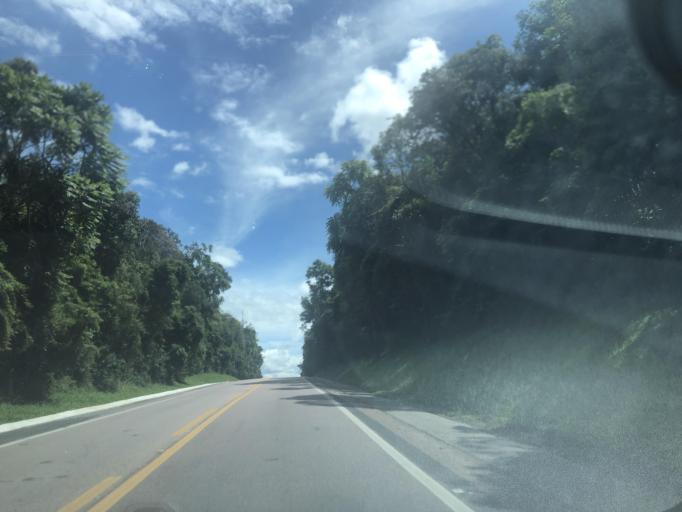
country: BR
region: Santa Catarina
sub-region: Mafra
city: Mafra
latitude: -26.3082
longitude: -49.9587
